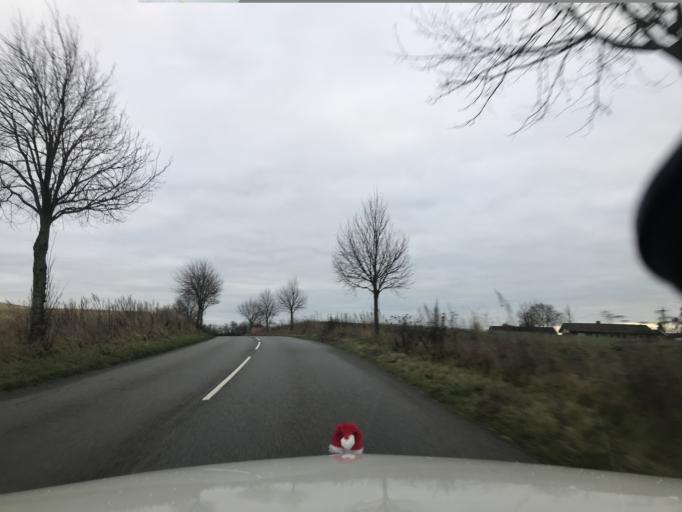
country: DK
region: South Denmark
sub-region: Sonderborg Kommune
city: Broager
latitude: 54.8901
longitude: 9.6855
